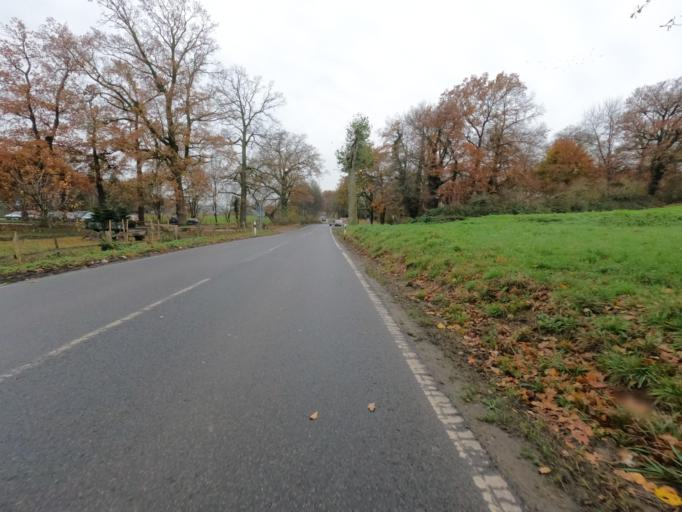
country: DE
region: North Rhine-Westphalia
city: Geilenkirchen
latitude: 50.9732
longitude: 6.1329
